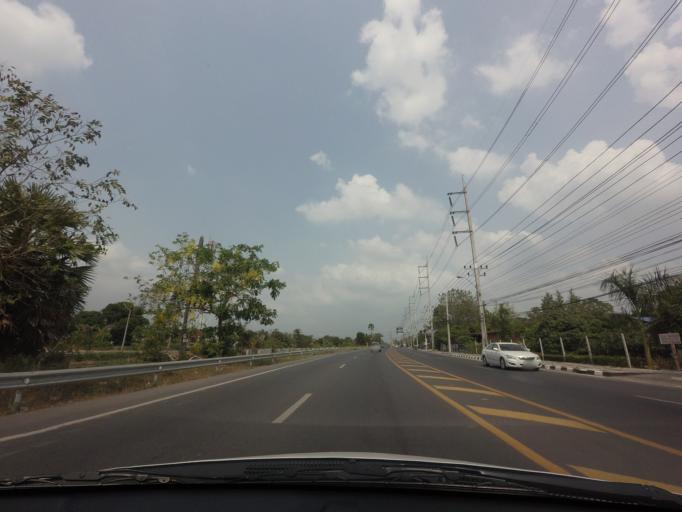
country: TH
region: Pathum Thani
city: Thanyaburi
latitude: 14.0468
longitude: 100.7101
